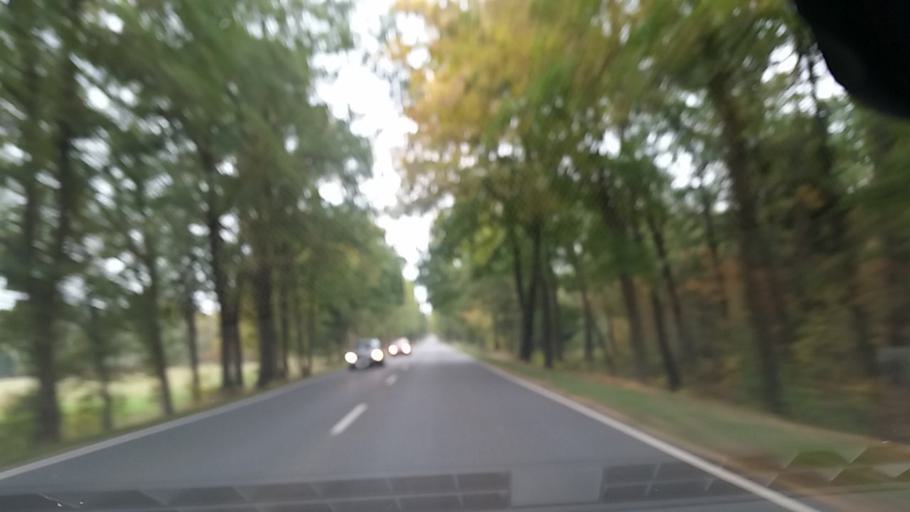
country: DE
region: Lower Saxony
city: Gross Oesingen
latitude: 52.6249
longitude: 10.4752
